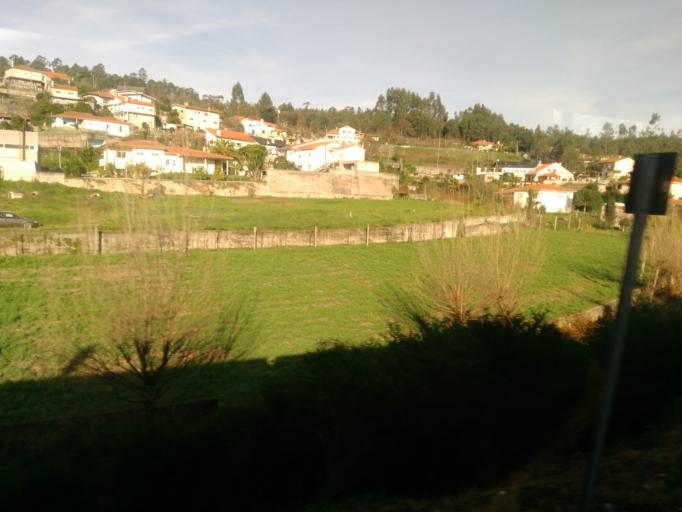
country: PT
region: Braga
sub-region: Braga
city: Oliveira
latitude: 41.4987
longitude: -8.4953
